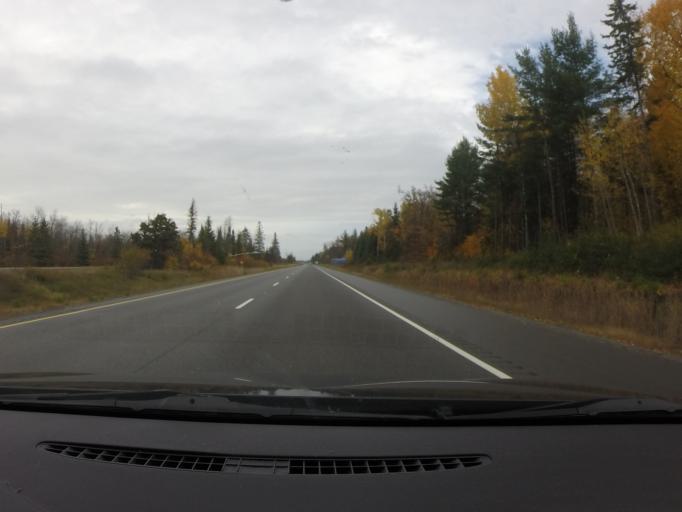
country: CA
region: Ontario
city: Carleton Place
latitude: 45.3185
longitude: -76.0872
